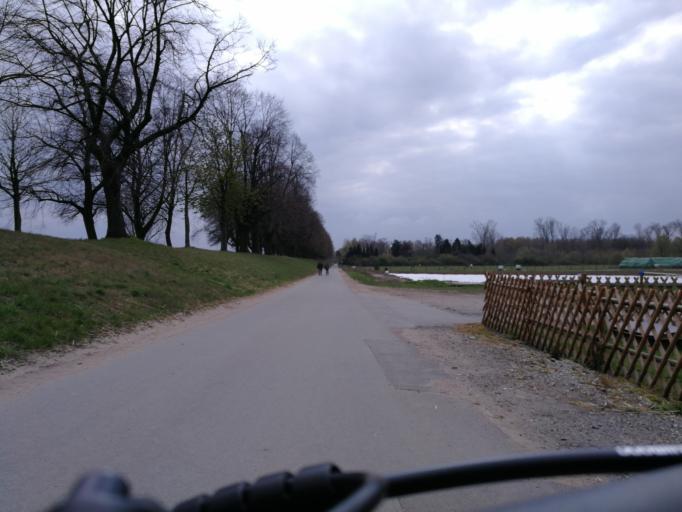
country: DE
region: North Rhine-Westphalia
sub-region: Regierungsbezirk Dusseldorf
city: Neuss
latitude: 51.1968
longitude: 6.7256
